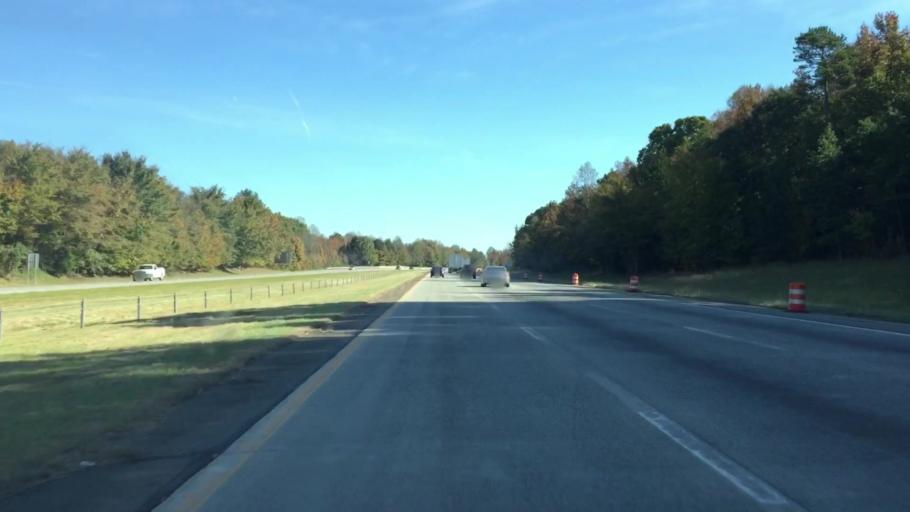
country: US
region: North Carolina
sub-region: Davidson County
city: Thomasville
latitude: 35.8574
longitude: -80.0877
